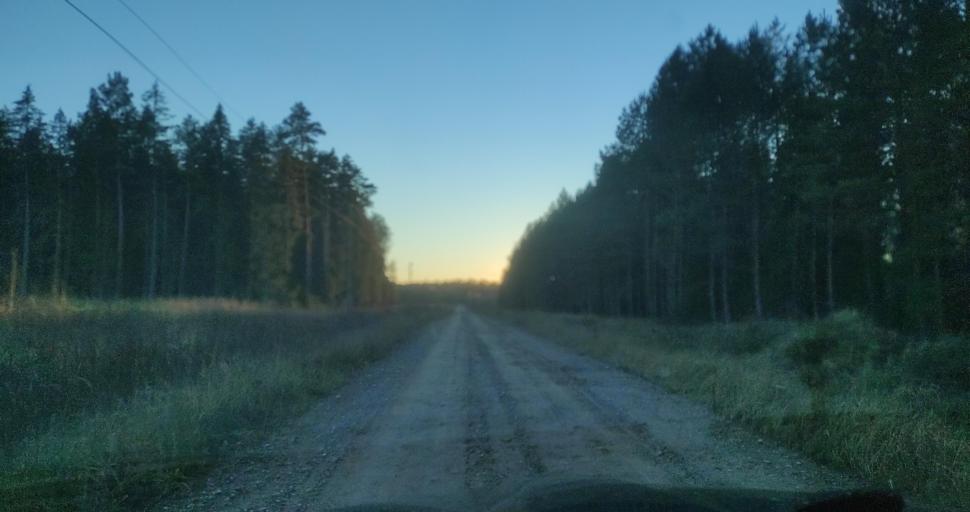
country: LV
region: Dundaga
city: Dundaga
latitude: 57.3706
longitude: 22.0735
